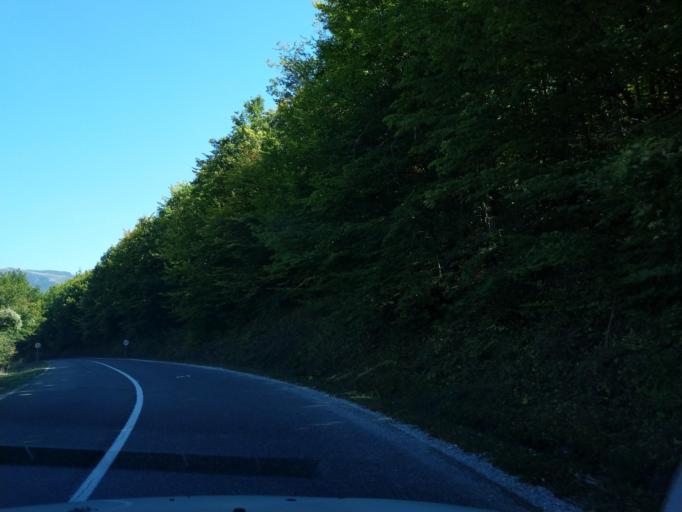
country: RS
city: Sokolovica
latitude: 43.2545
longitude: 20.2493
